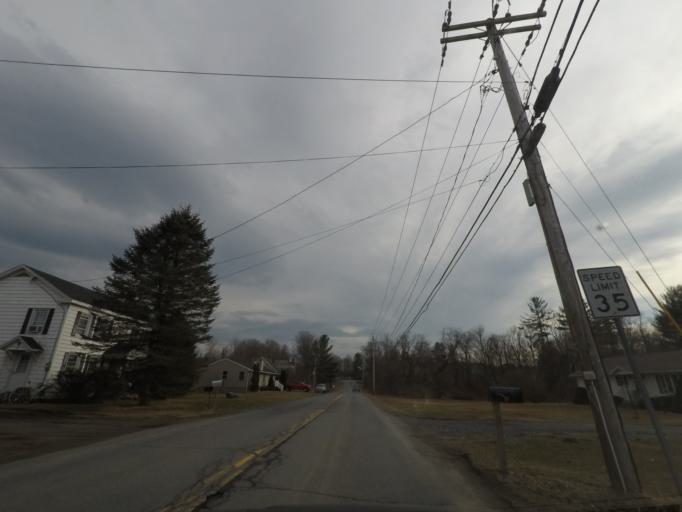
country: US
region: New York
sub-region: Washington County
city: Cambridge
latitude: 42.9554
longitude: -73.4331
